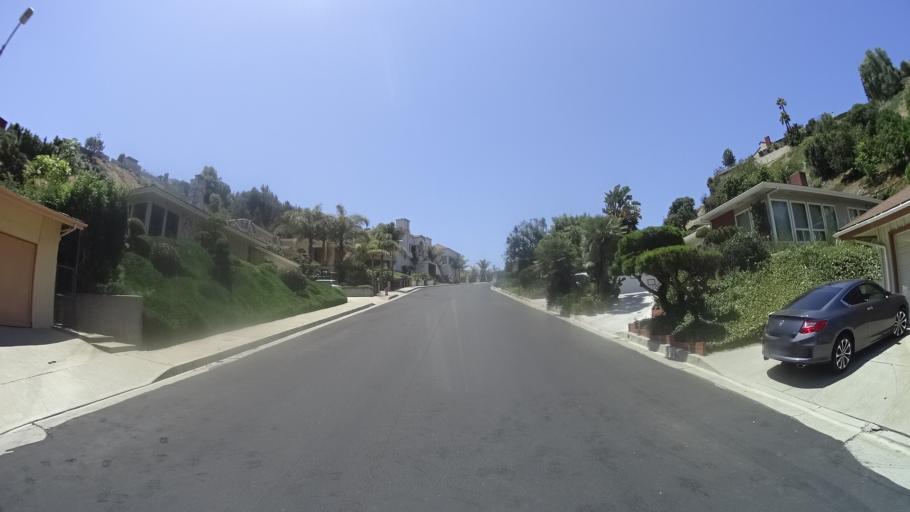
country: US
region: California
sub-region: Los Angeles County
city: View Park-Windsor Hills
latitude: 34.0140
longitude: -118.3619
